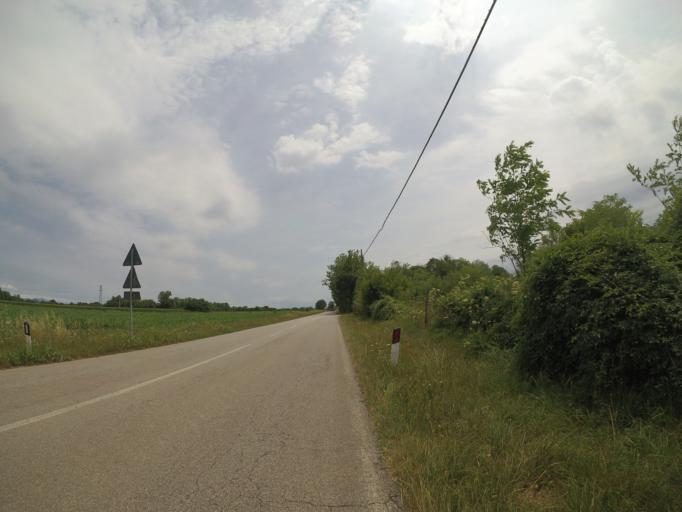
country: IT
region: Friuli Venezia Giulia
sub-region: Provincia di Udine
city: Sedegliano
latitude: 46.0060
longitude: 12.9842
